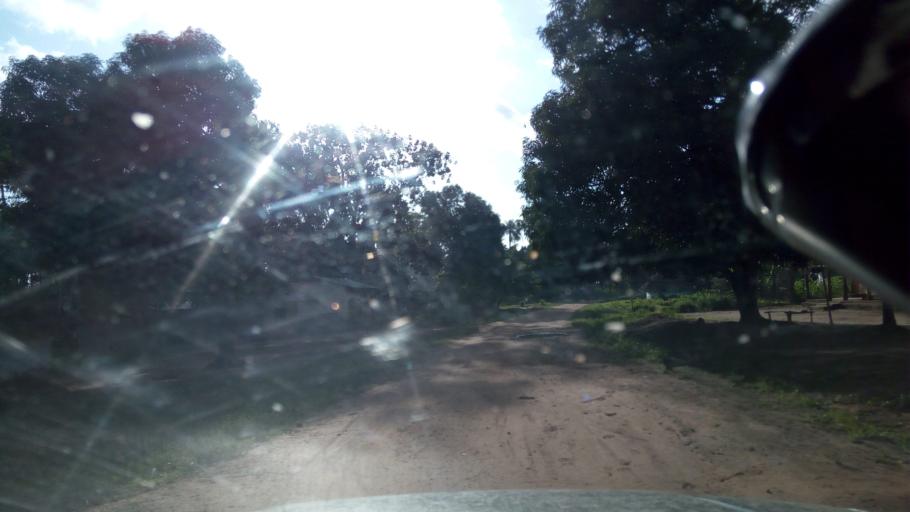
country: SL
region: Northern Province
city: Sawkta
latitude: 8.6998
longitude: -13.1143
